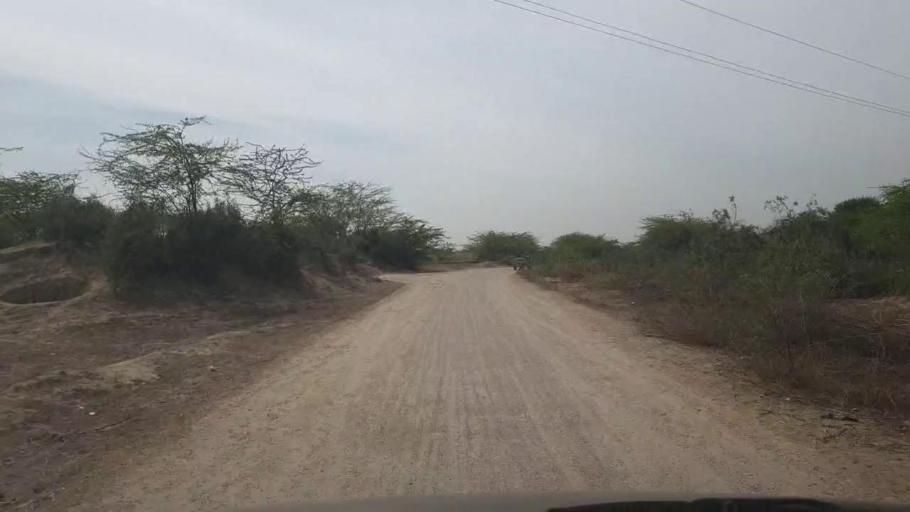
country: PK
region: Sindh
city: Umarkot
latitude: 25.2450
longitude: 69.7167
